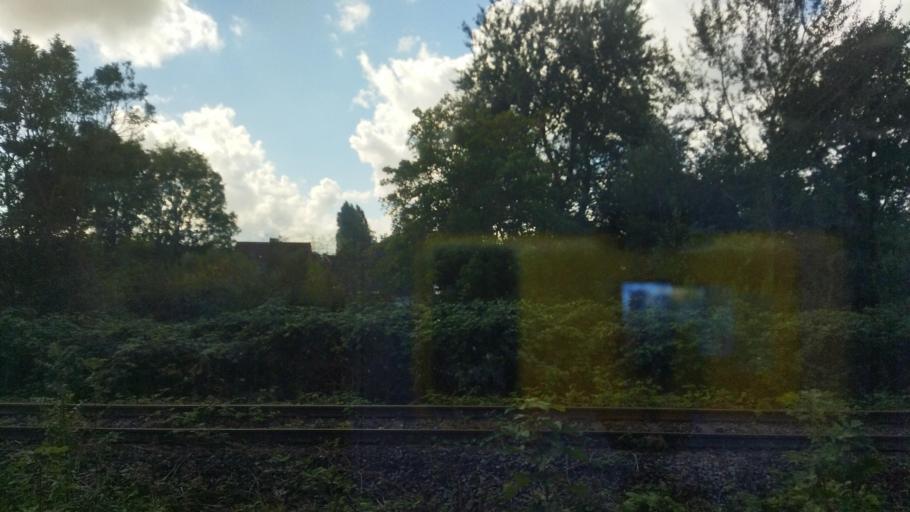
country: DE
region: Lower Saxony
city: Emden
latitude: 53.3567
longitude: 7.2235
